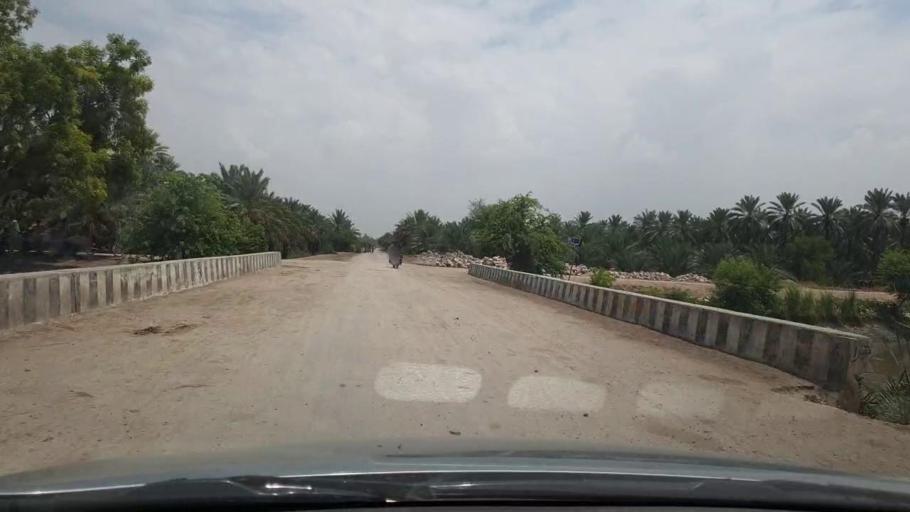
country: PK
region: Sindh
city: Khairpur
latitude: 27.4320
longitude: 68.7754
